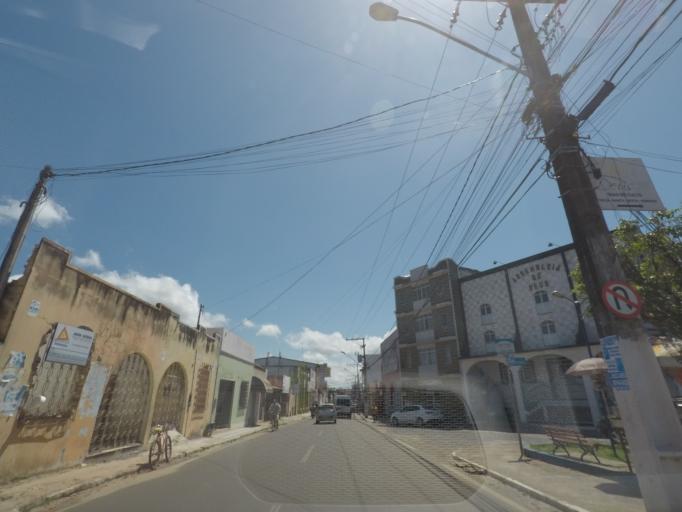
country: BR
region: Bahia
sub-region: Valenca
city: Valenca
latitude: -13.3666
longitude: -39.0704
